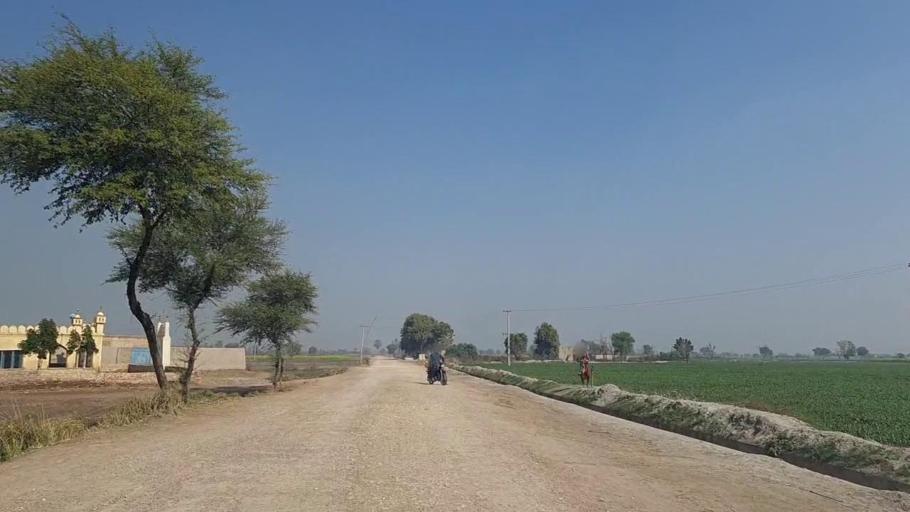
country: PK
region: Sindh
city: Nawabshah
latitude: 26.2289
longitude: 68.4912
